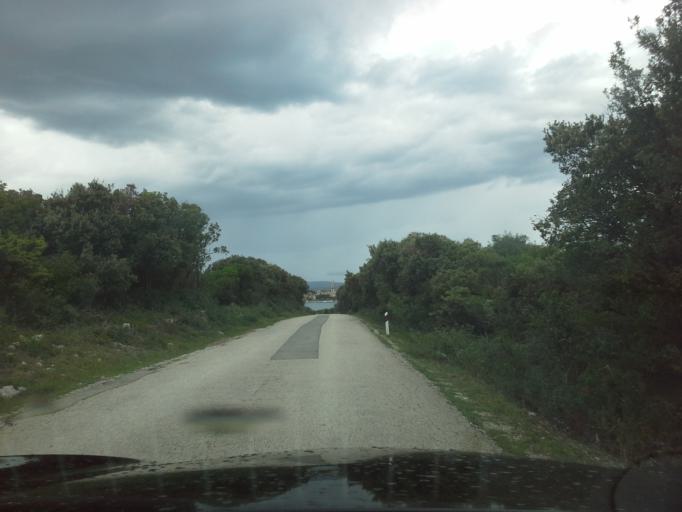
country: HR
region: Primorsko-Goranska
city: Mali Losinj
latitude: 44.6837
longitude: 14.3944
